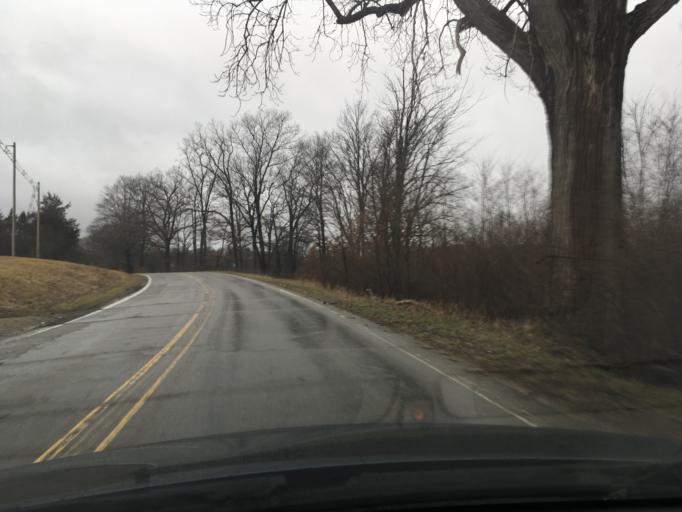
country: US
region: Michigan
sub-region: Jackson County
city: Grass Lake
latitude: 42.3111
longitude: -84.1423
